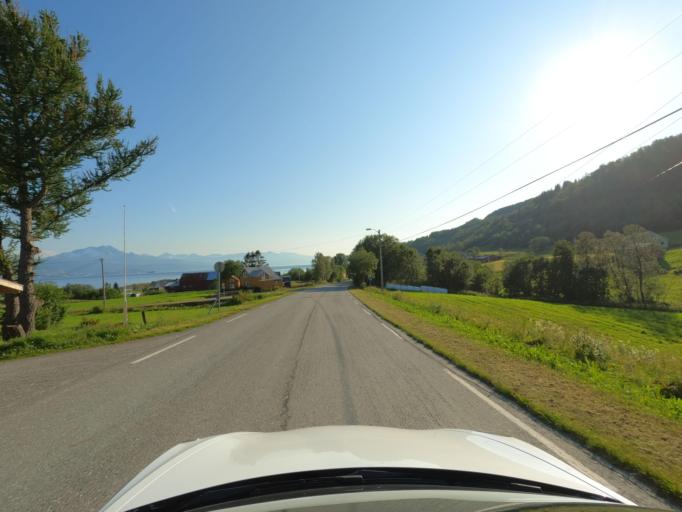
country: NO
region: Nordland
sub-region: Narvik
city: Bjerkvik
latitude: 68.5324
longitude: 17.4756
